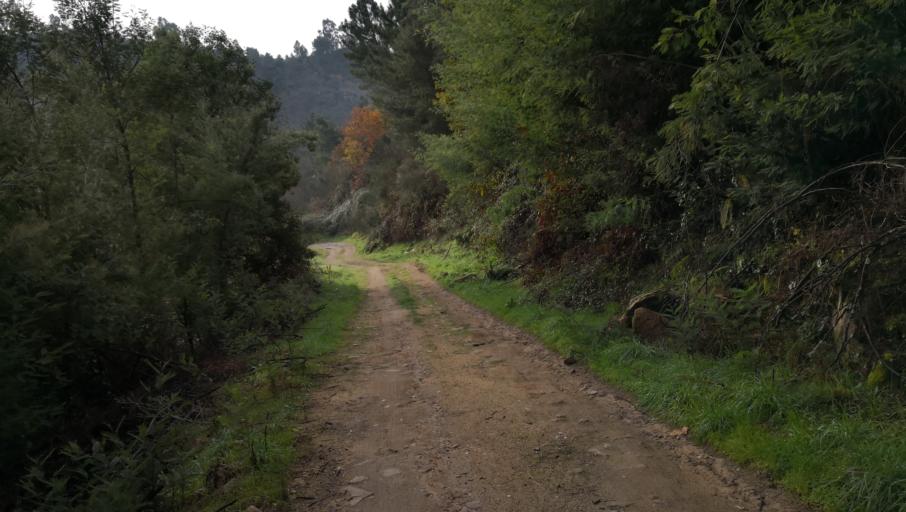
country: PT
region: Vila Real
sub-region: Vila Real
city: Vila Real
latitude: 41.2893
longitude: -7.7493
